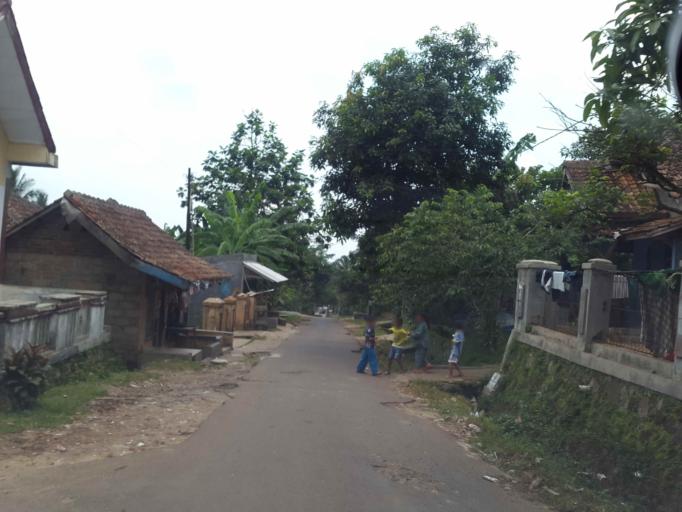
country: ID
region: Banten
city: Cilaja
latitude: -6.3133
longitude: 106.0845
